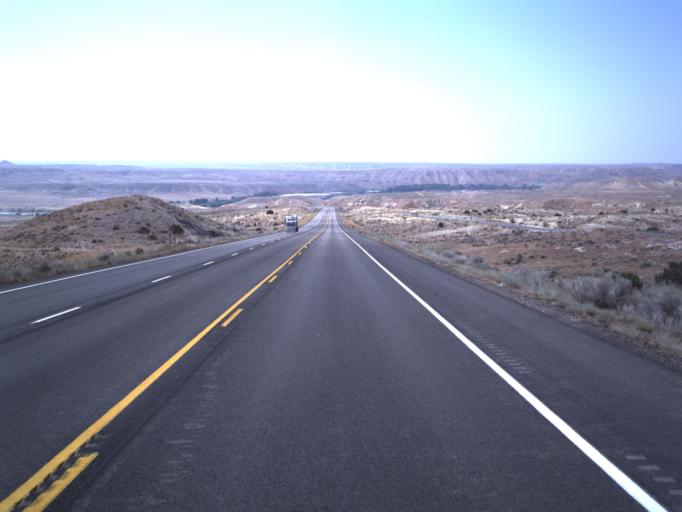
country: US
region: Utah
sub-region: Uintah County
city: Naples
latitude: 40.3373
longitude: -109.4848
